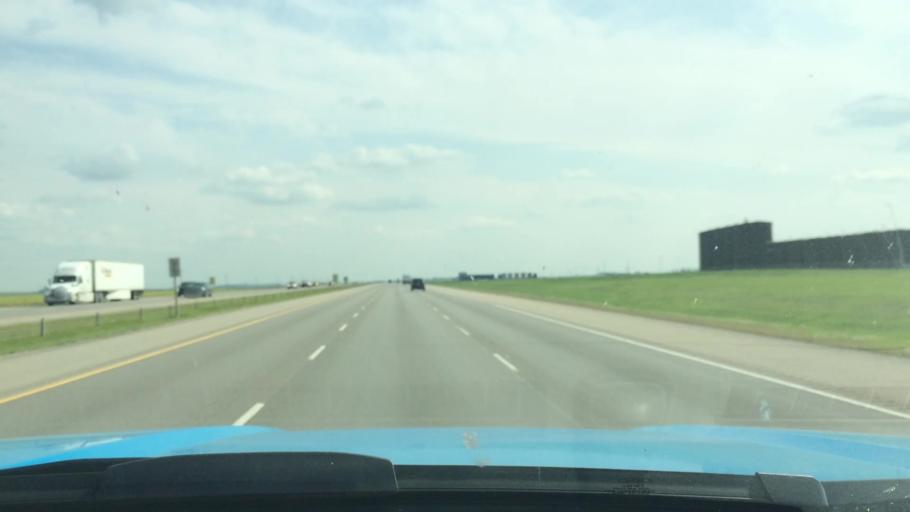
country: CA
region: Alberta
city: Crossfield
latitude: 51.5037
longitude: -114.0254
